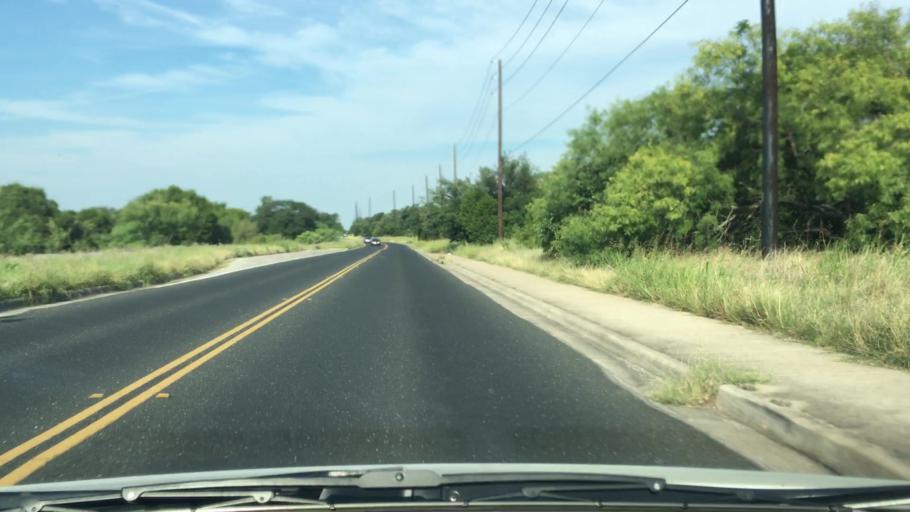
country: US
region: Texas
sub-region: Williamson County
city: Anderson Mill
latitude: 30.4866
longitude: -97.7762
